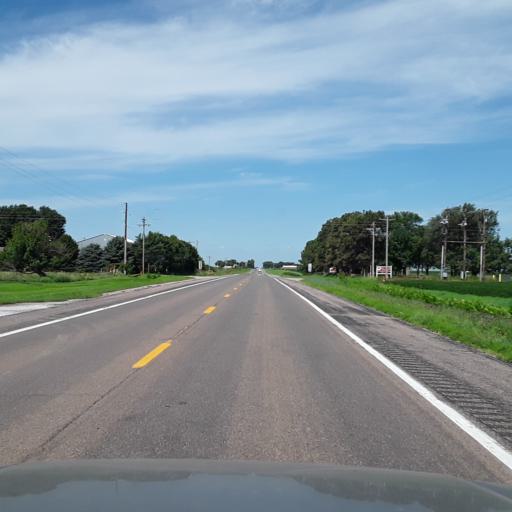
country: US
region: Nebraska
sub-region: Seward County
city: Seward
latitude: 40.9017
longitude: -97.1566
